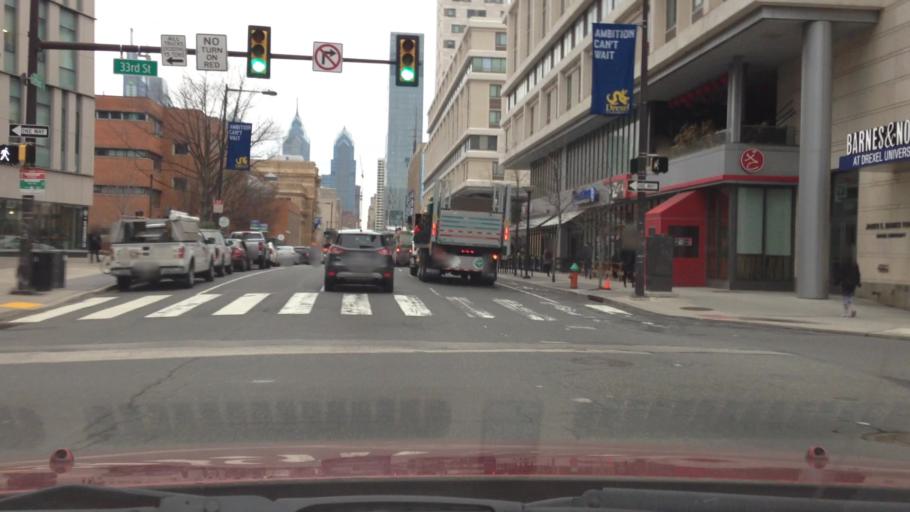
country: US
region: Pennsylvania
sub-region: Philadelphia County
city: Philadelphia
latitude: 39.9541
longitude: -75.1890
